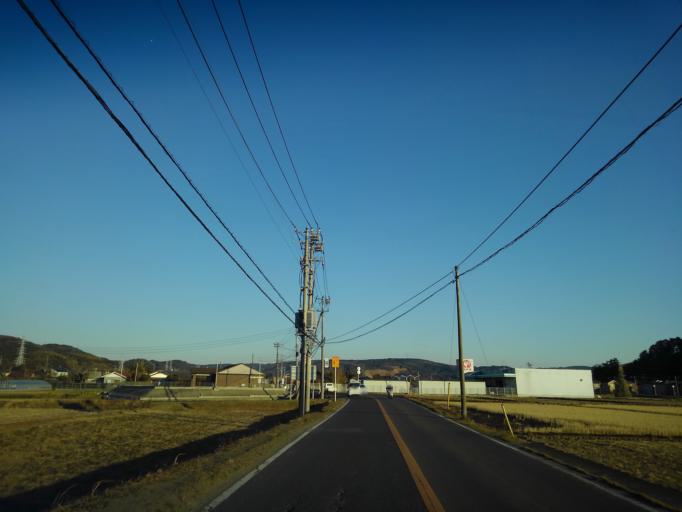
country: JP
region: Chiba
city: Kimitsu
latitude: 35.3049
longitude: 139.9630
